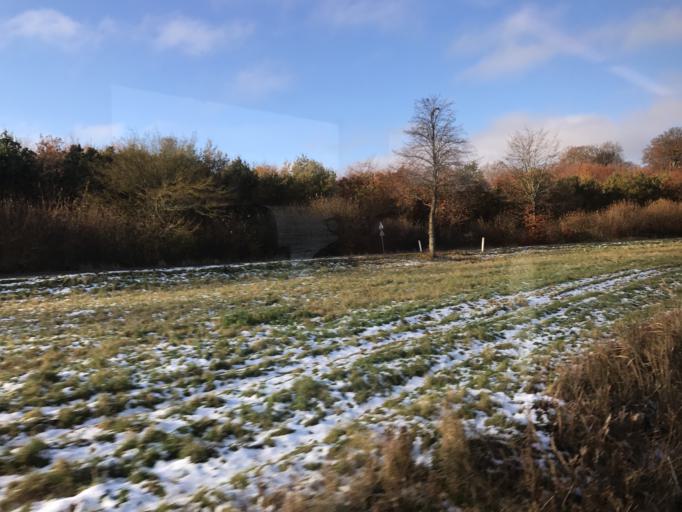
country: DK
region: Zealand
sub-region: Stevns Kommune
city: Harlev
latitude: 55.3830
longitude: 12.1962
